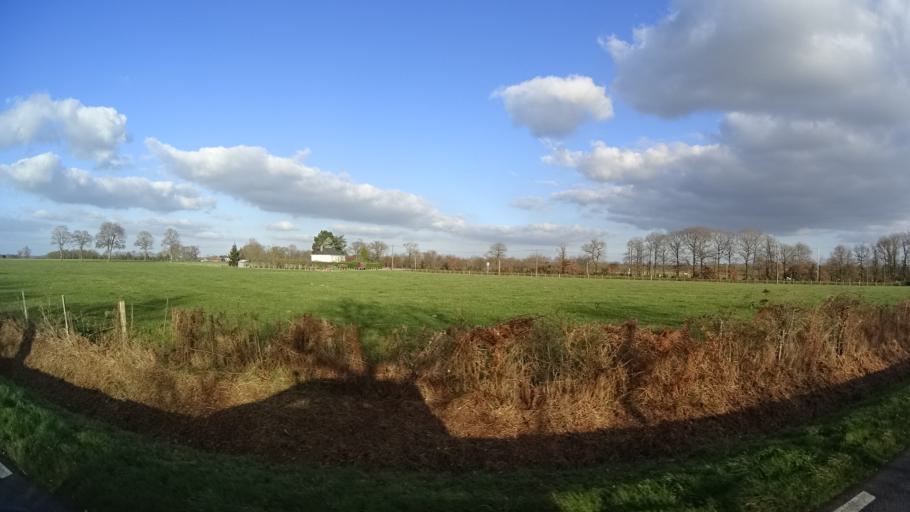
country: FR
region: Pays de la Loire
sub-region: Departement de la Loire-Atlantique
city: Plesse
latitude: 47.5161
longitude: -1.8880
